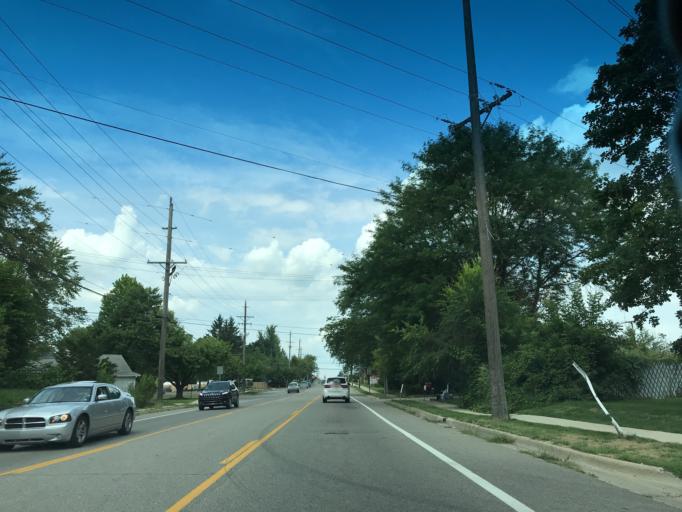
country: US
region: Michigan
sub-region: Washtenaw County
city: Ypsilanti
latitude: 42.2472
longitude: -83.6610
